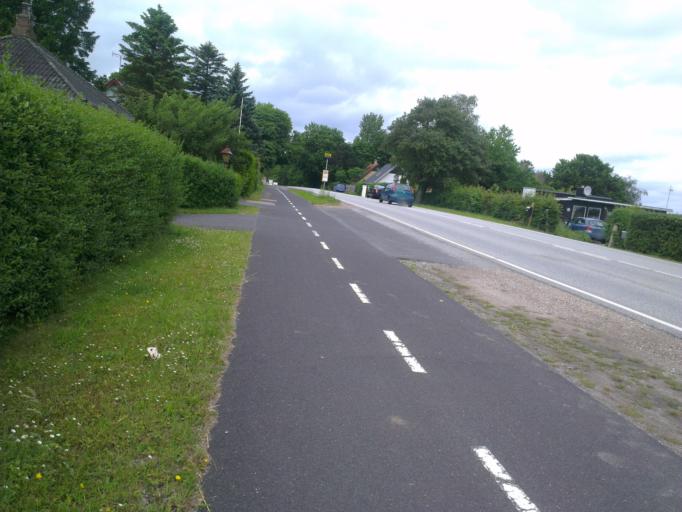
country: DK
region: Capital Region
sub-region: Frederikssund Kommune
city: Skibby
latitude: 55.6863
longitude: 11.9480
